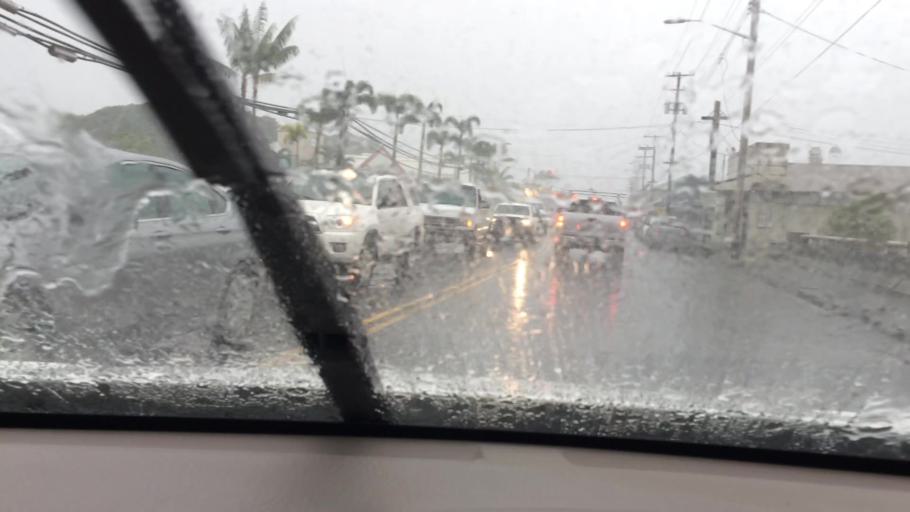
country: US
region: Hawaii
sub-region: Hawaii County
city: Hilo
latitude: 19.7216
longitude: -155.0848
